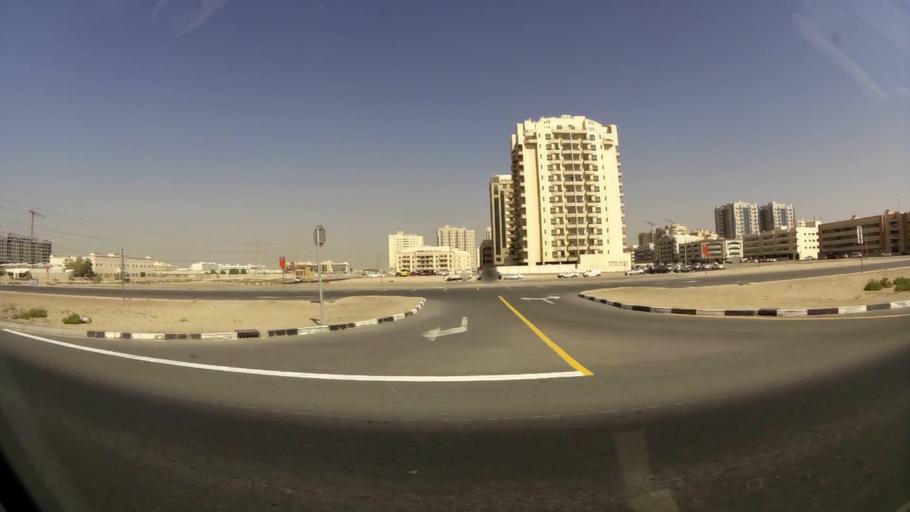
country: AE
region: Ash Shariqah
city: Sharjah
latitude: 25.2783
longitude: 55.3761
